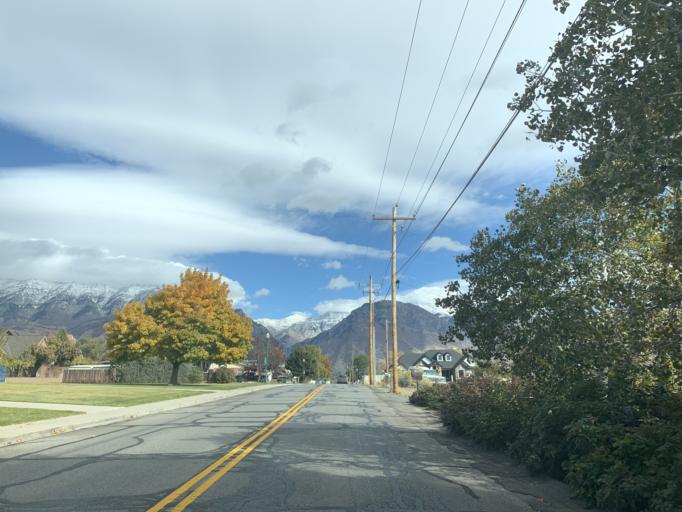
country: US
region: Utah
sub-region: Utah County
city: Orem
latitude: 40.2606
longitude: -111.6921
